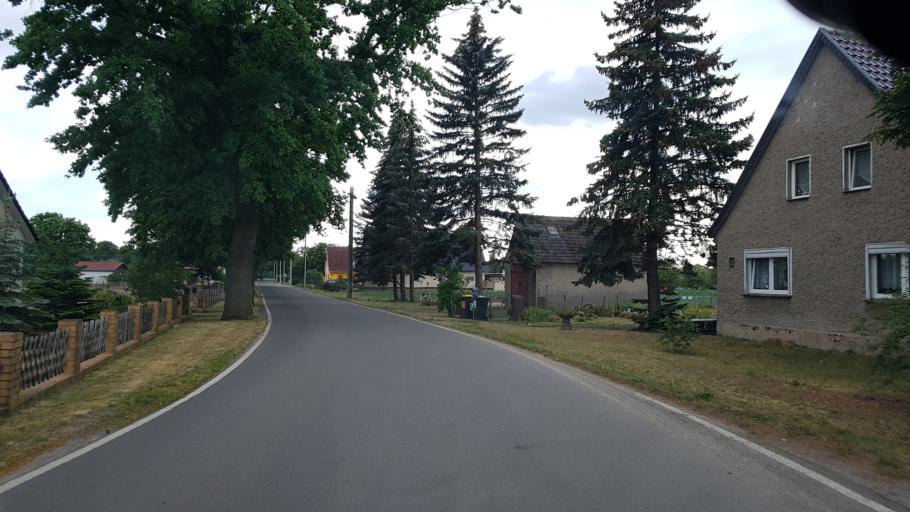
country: DE
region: Brandenburg
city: Kasel-Golzig
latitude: 51.9584
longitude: 13.6701
